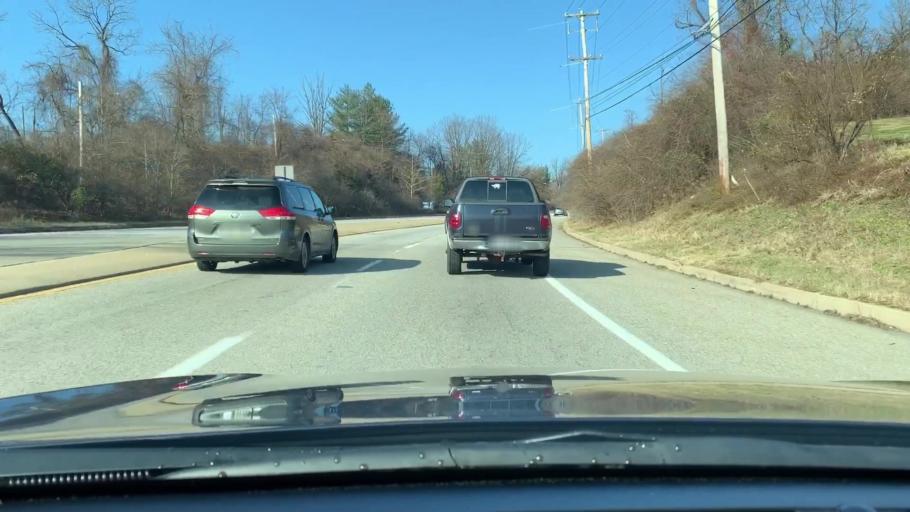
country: US
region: Pennsylvania
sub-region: Chester County
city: Malvern
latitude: 40.0607
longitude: -75.5332
